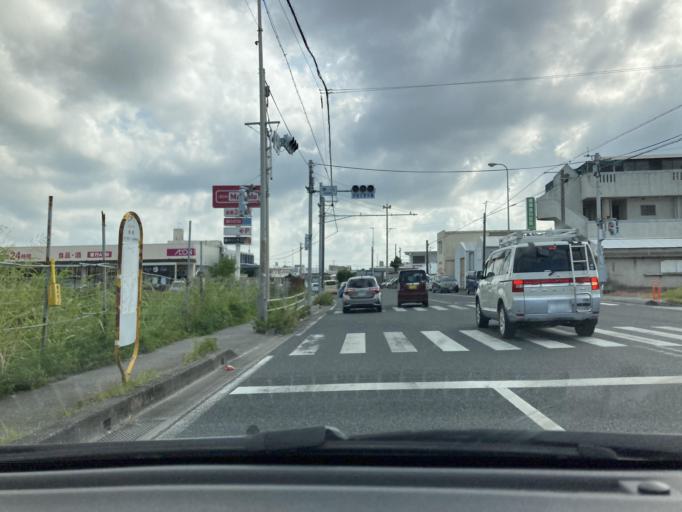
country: JP
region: Okinawa
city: Ginowan
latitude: 26.2179
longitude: 127.7642
